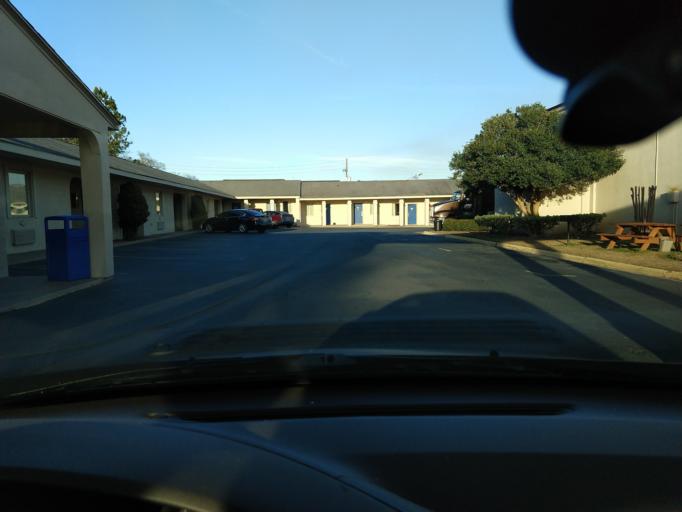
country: US
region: Georgia
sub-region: Sumter County
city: Americus
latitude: 32.0749
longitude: -84.2439
